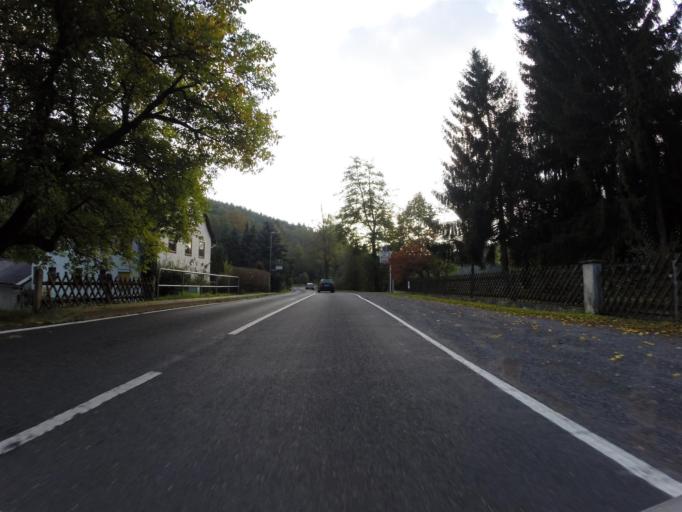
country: DE
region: Thuringia
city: Trockenborn-Wolfersdorf
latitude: 50.7997
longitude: 11.7052
